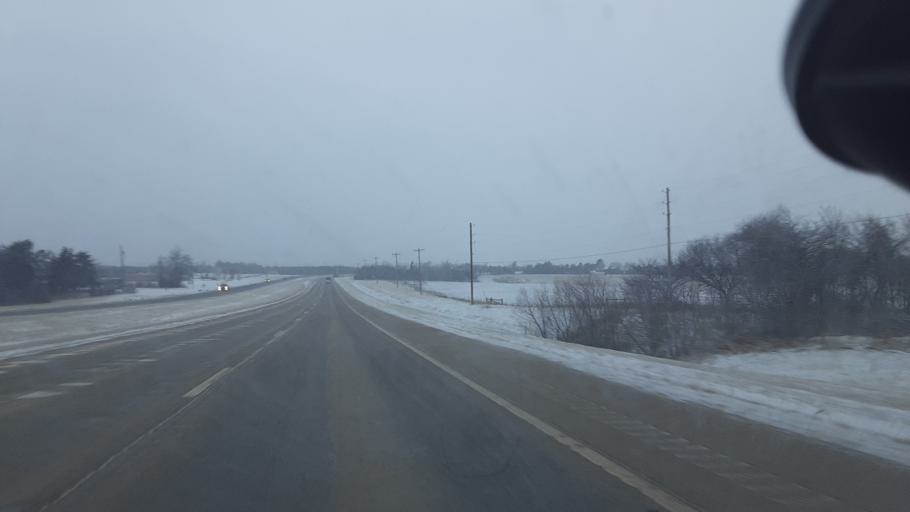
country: US
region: Oklahoma
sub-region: Logan County
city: Guthrie
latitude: 35.8903
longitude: -97.3655
